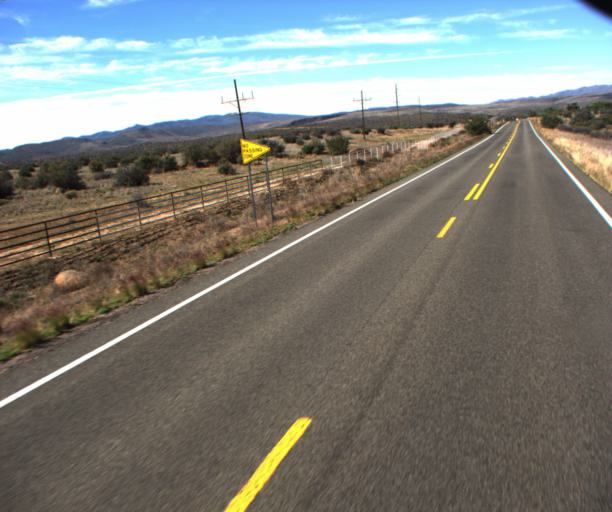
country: US
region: Arizona
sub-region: Yavapai County
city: Prescott
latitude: 34.3764
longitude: -112.6606
